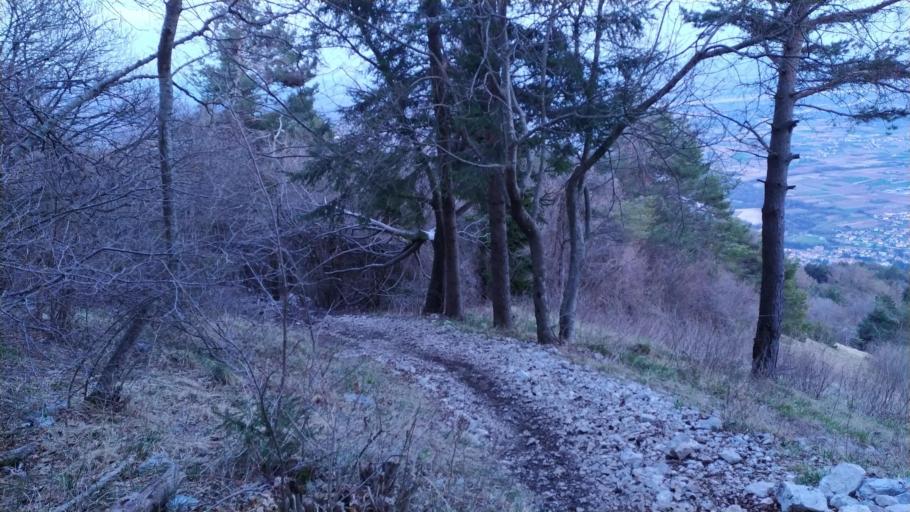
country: IT
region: Friuli Venezia Giulia
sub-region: Provincia di Pordenone
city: Maniago
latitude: 46.1877
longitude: 12.6895
